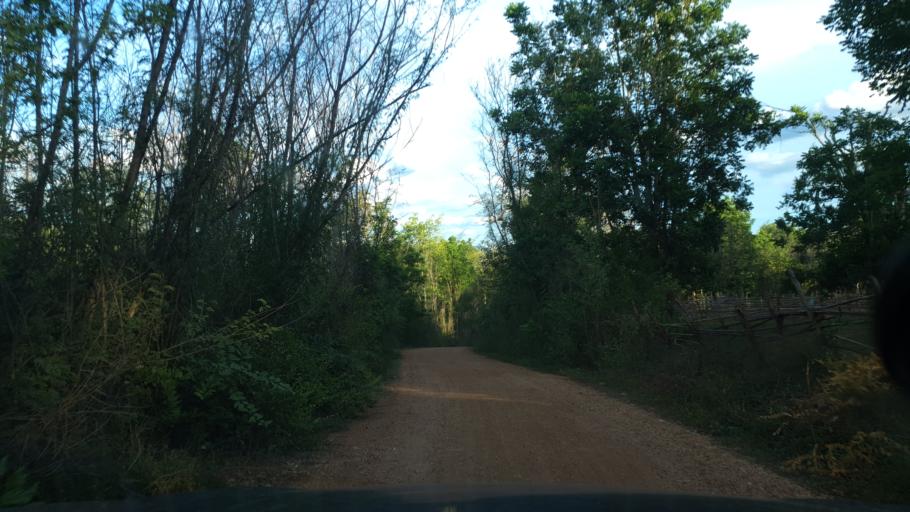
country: TH
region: Lampang
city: Sop Prap
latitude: 17.9550
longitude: 99.3481
